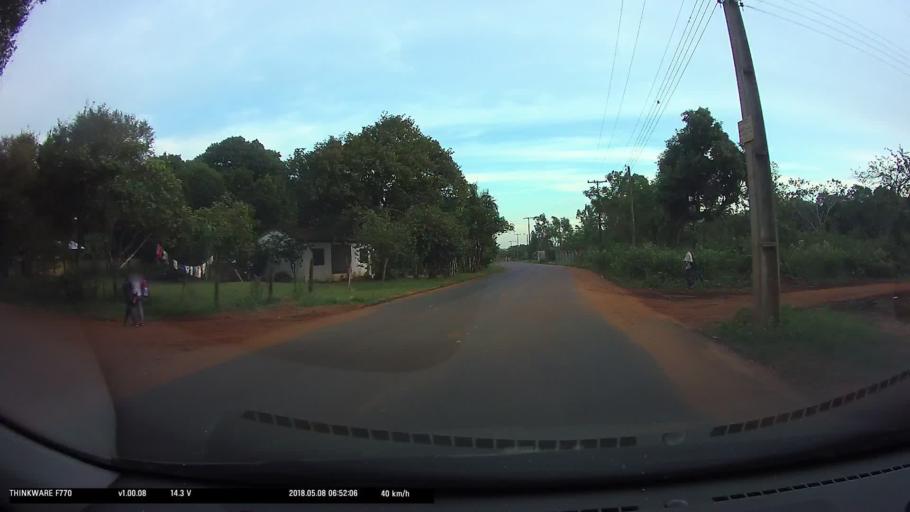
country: PY
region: Central
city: Limpio
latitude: -25.2385
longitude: -57.4642
